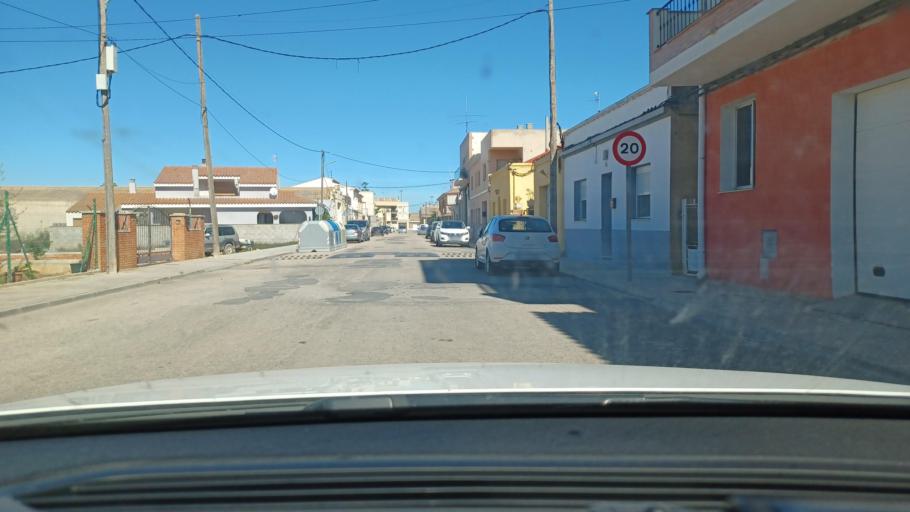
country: ES
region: Catalonia
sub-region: Provincia de Tarragona
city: Deltebre
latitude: 40.7182
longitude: 0.7399
